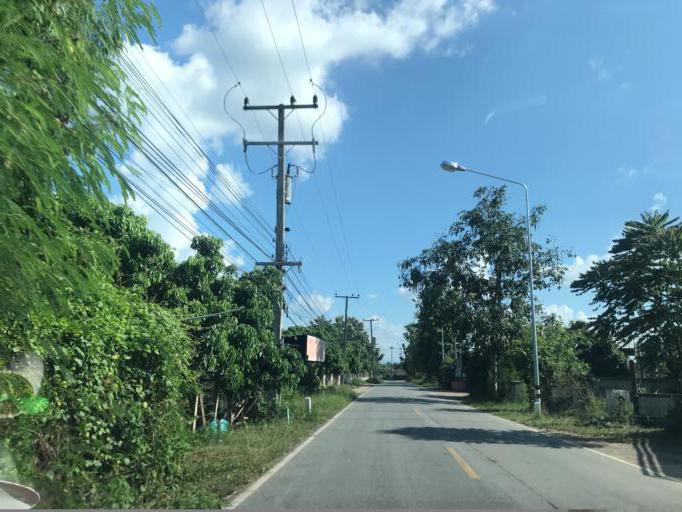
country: TH
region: Lamphun
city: Pa Sang
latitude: 18.5334
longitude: 98.8426
